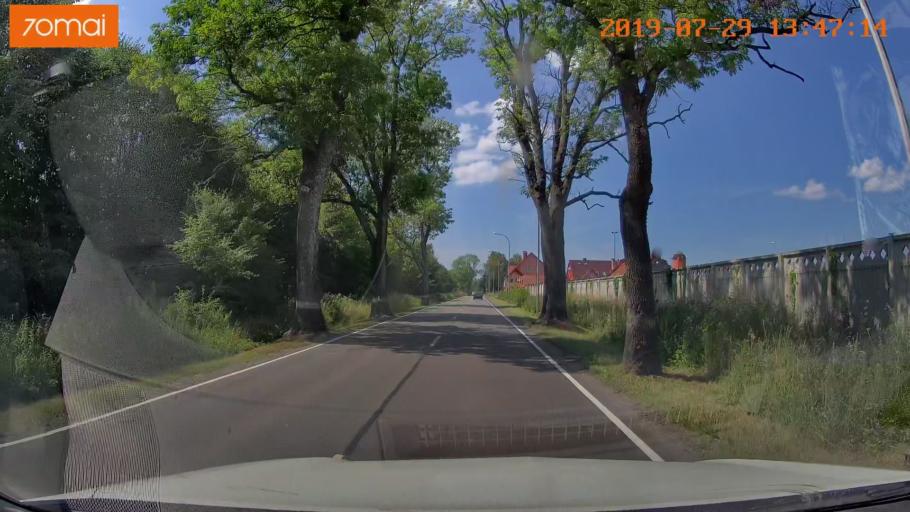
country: RU
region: Kaliningrad
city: Primorsk
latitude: 54.7399
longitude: 20.0517
